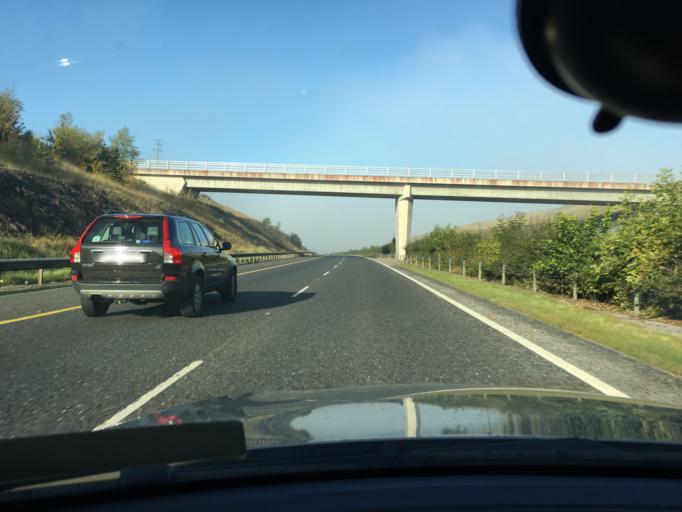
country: IE
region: Leinster
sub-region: An Mhi
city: Enfield
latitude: 53.4117
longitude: -6.7520
